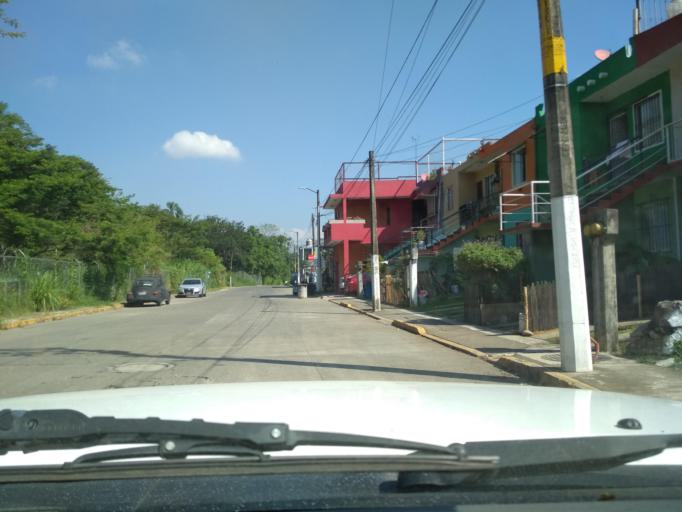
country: MX
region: Veracruz
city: Amatlan de los Reyes
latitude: 18.8707
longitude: -96.9074
